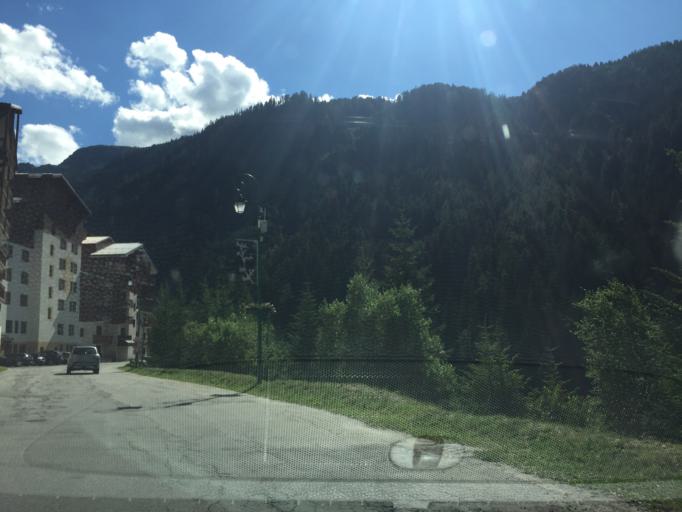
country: FR
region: Rhone-Alpes
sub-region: Departement de la Savoie
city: Modane
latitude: 45.1742
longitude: 6.6531
